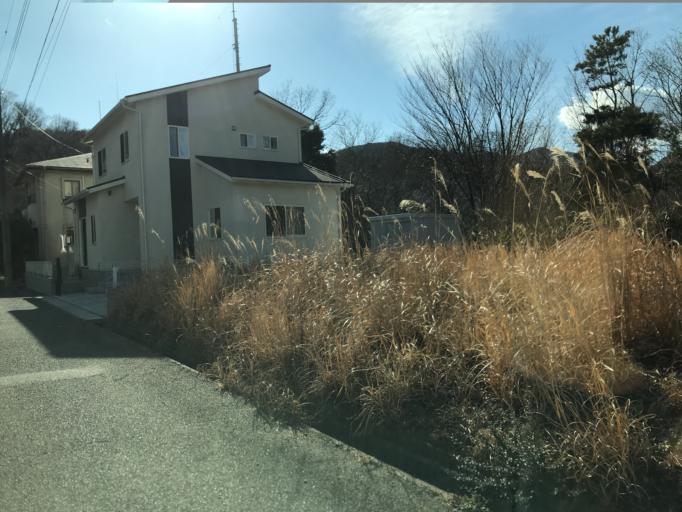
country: JP
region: Fukushima
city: Iwaki
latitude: 37.1248
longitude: 140.8424
